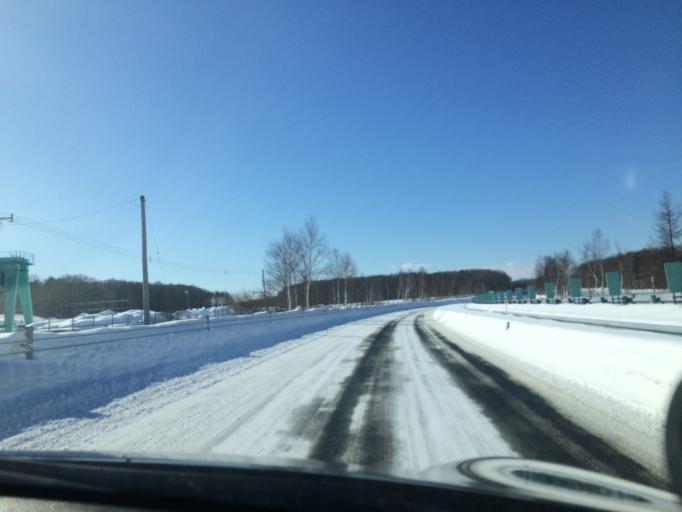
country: JP
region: Hokkaido
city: Chitose
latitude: 42.8554
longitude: 141.6028
